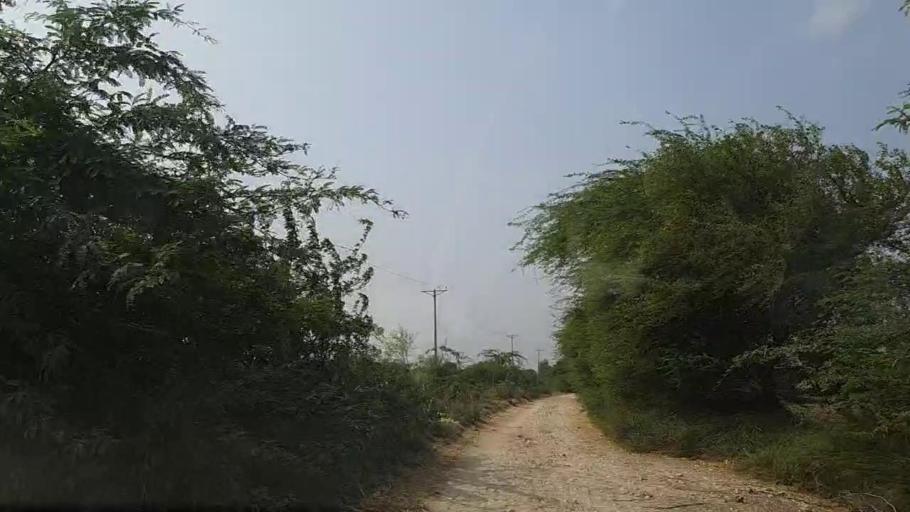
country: PK
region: Sindh
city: Mirpur Sakro
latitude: 24.6161
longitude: 67.7373
